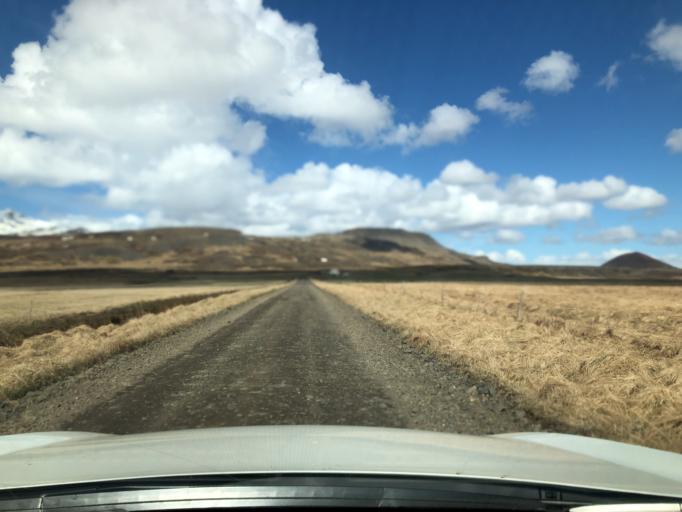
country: IS
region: West
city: Stykkisholmur
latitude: 64.8488
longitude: -22.3706
